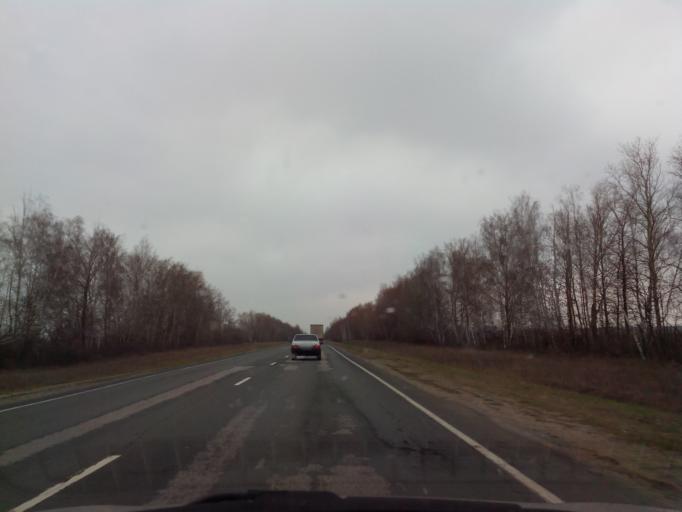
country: RU
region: Tambov
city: Pervomayskiy
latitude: 53.1003
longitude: 40.3949
